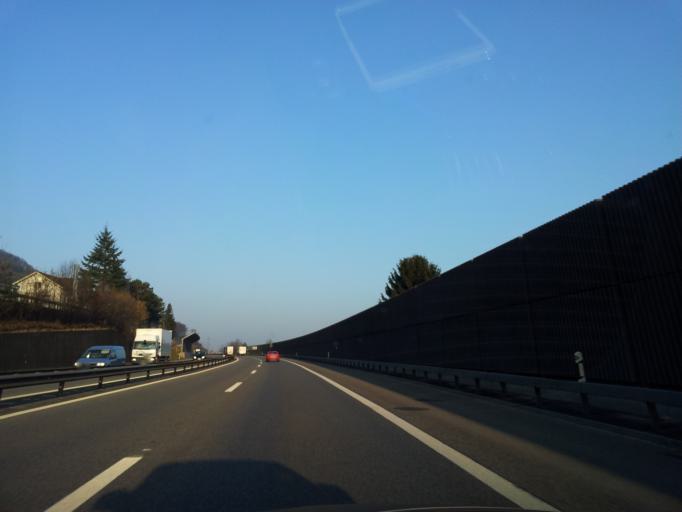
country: CH
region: Aargau
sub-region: Bezirk Rheinfelden
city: Stein
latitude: 47.5419
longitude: 7.9501
